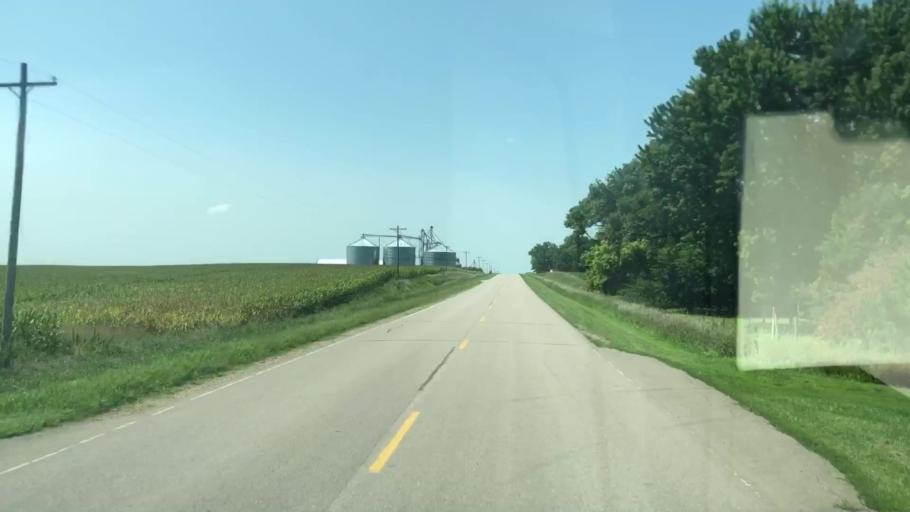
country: US
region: Iowa
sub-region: O'Brien County
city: Sheldon
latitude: 43.2443
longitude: -95.7669
